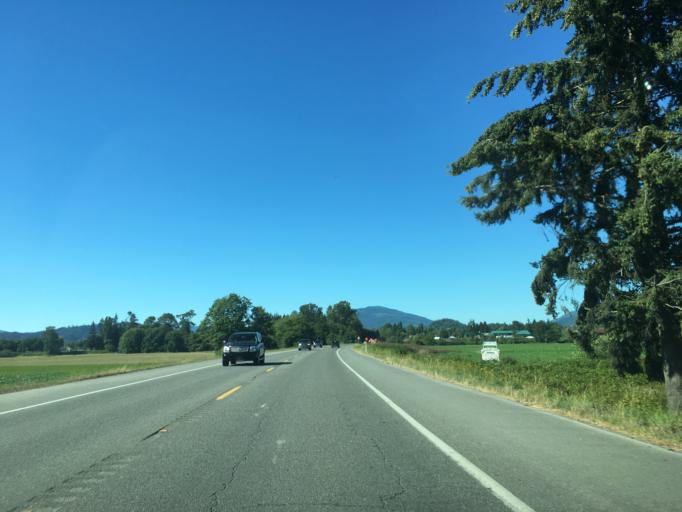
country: US
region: Washington
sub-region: Skagit County
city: Sedro-Woolley
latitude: 48.4921
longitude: -122.2467
